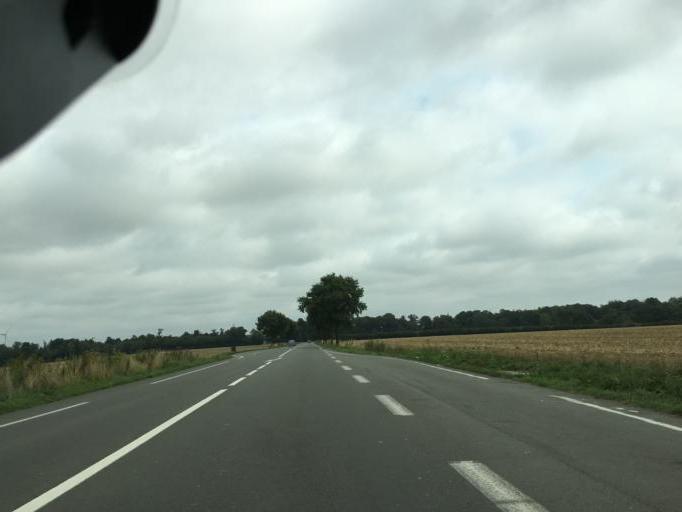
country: FR
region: Nord-Pas-de-Calais
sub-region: Departement du Pas-de-Calais
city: Saint-Pol-sur-Ternoise
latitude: 50.4067
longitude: 2.3673
